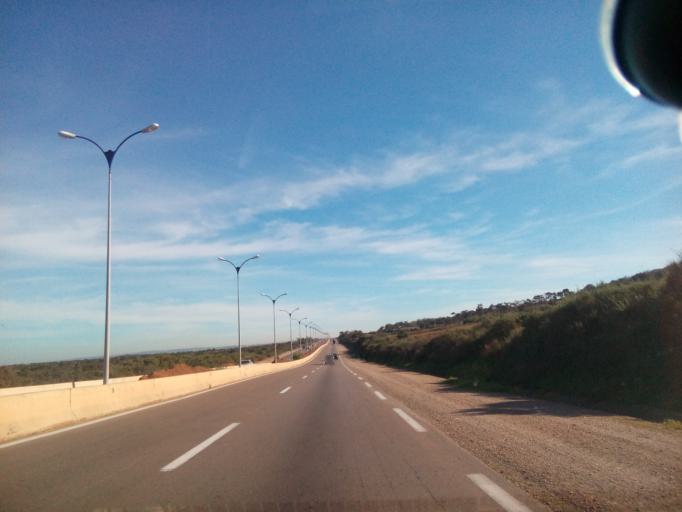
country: DZ
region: Mostaganem
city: Mostaganem
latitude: 35.8002
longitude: -0.0797
